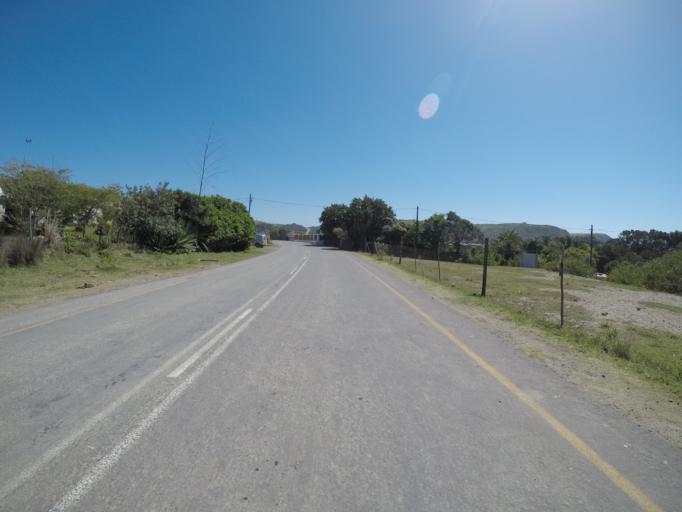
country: ZA
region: Eastern Cape
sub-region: OR Tambo District Municipality
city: Libode
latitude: -31.9850
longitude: 29.1486
